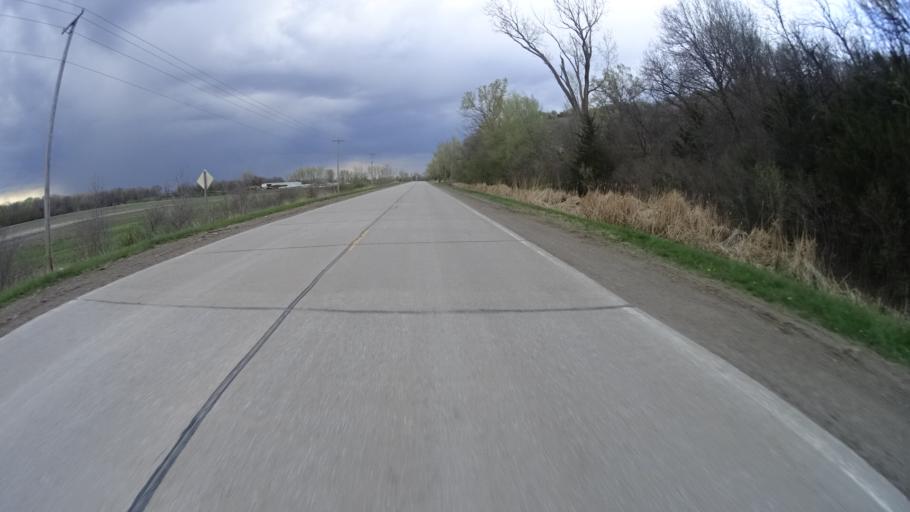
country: US
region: Iowa
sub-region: Mills County
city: Glenwood
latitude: 41.0759
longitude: -95.8131
